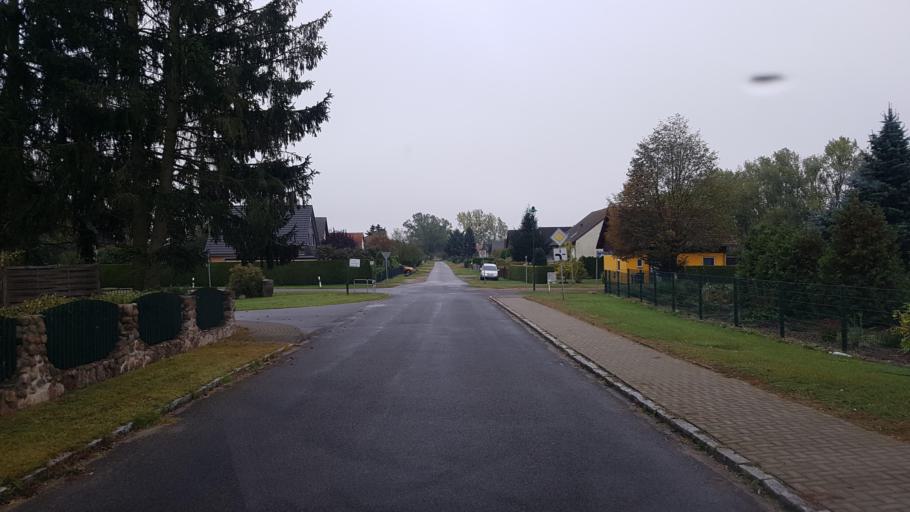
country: DE
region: Brandenburg
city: Furstenwalde
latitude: 52.4316
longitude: 14.0175
